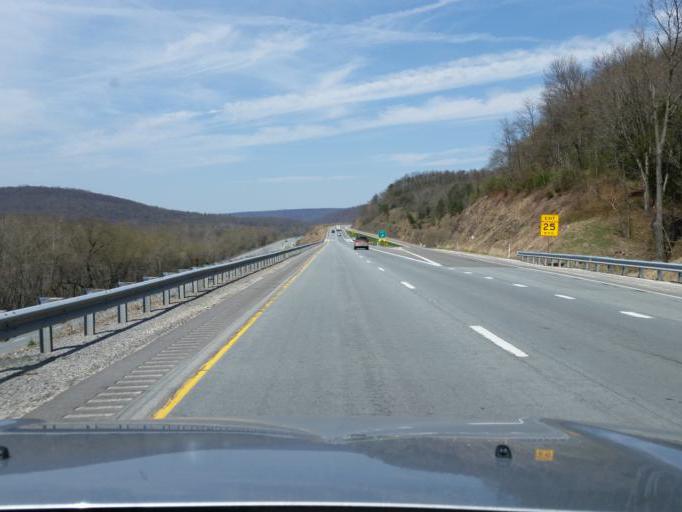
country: US
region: Pennsylvania
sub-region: Perry County
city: Duncannon
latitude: 40.4479
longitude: -77.0192
